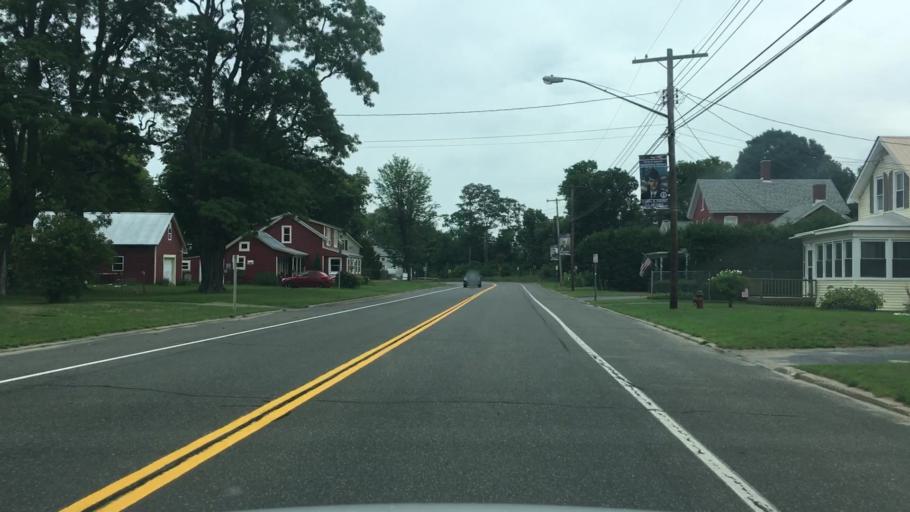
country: US
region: New York
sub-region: Essex County
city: Keeseville
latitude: 44.5022
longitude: -73.4879
